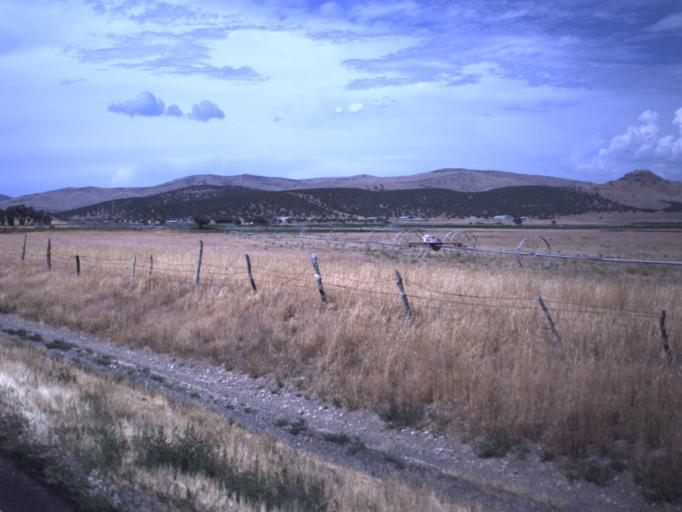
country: US
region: Utah
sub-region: Sanpete County
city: Fountain Green
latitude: 39.6130
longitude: -111.6279
